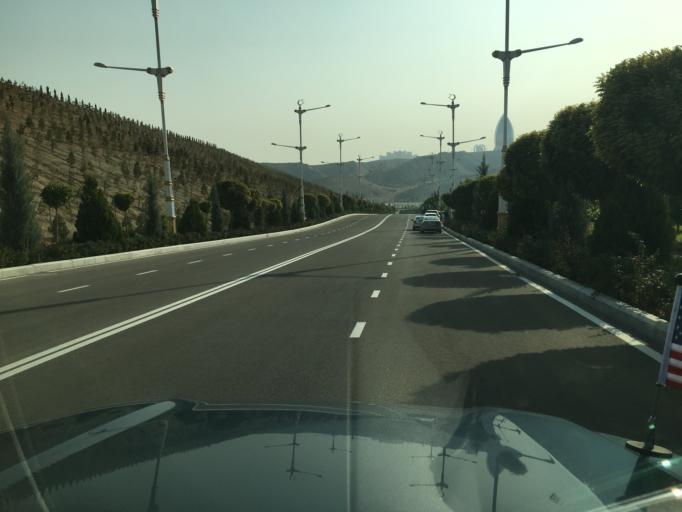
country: TM
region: Ahal
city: Ashgabat
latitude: 37.9383
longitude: 58.3150
